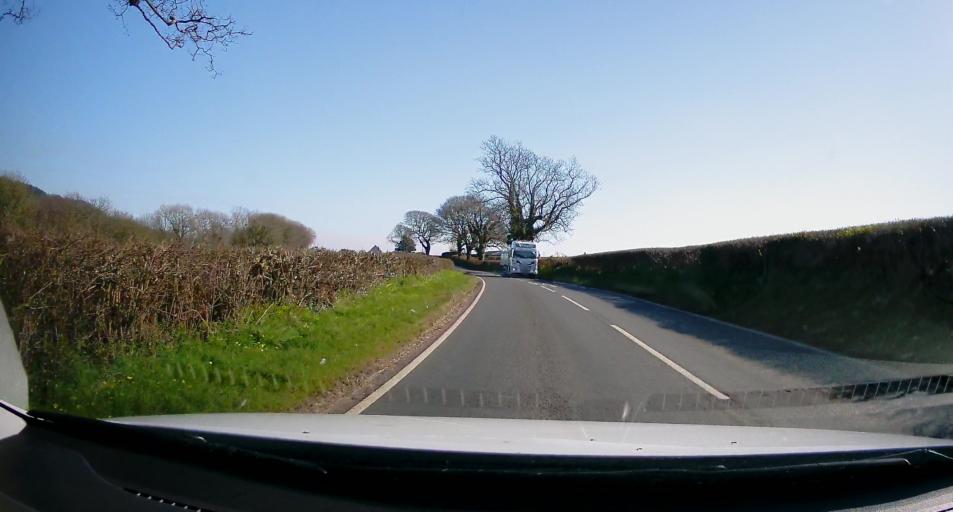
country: GB
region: Wales
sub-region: County of Ceredigion
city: Penparcau
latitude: 52.3740
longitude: -4.0726
